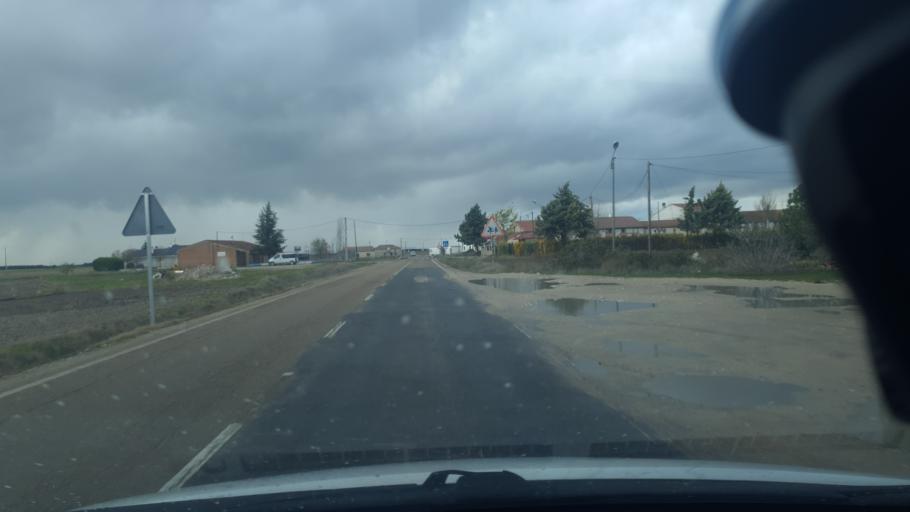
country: ES
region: Castille and Leon
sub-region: Provincia de Segovia
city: Sanchonuno
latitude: 41.3096
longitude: -4.3643
